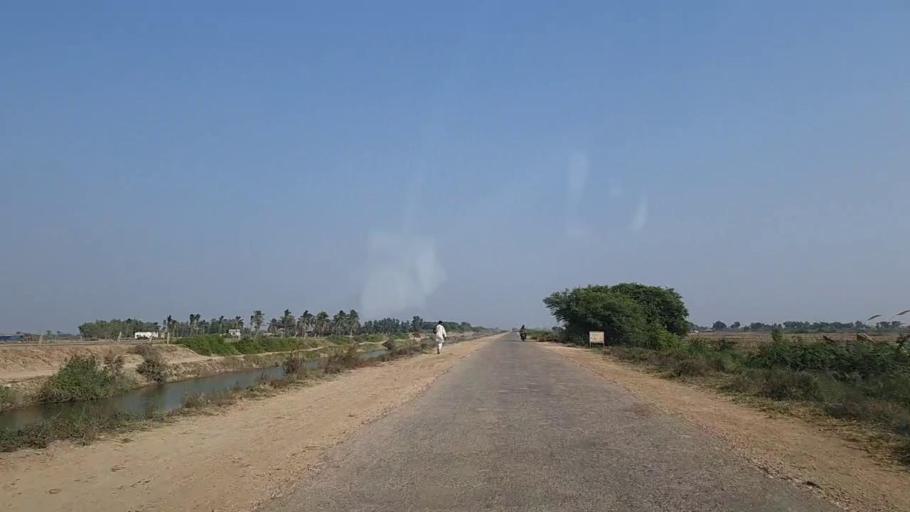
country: PK
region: Sindh
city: Mirpur Sakro
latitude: 24.6373
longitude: 67.5964
